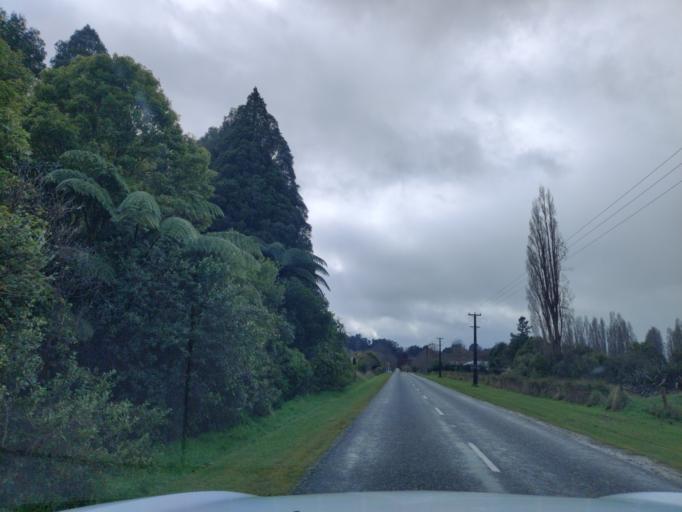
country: NZ
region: Manawatu-Wanganui
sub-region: Palmerston North City
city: Palmerston North
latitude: -40.1755
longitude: 175.7923
